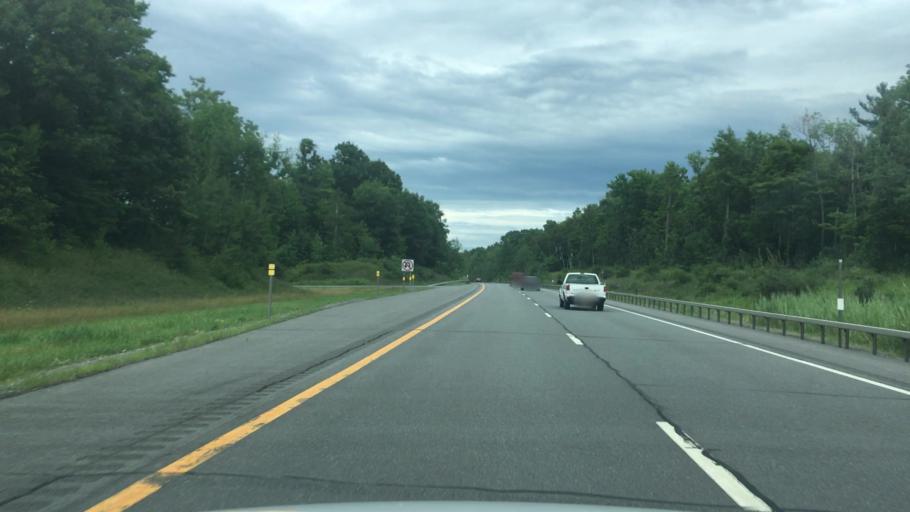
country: US
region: New York
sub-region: Schoharie County
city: Schoharie
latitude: 42.7238
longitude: -74.2263
